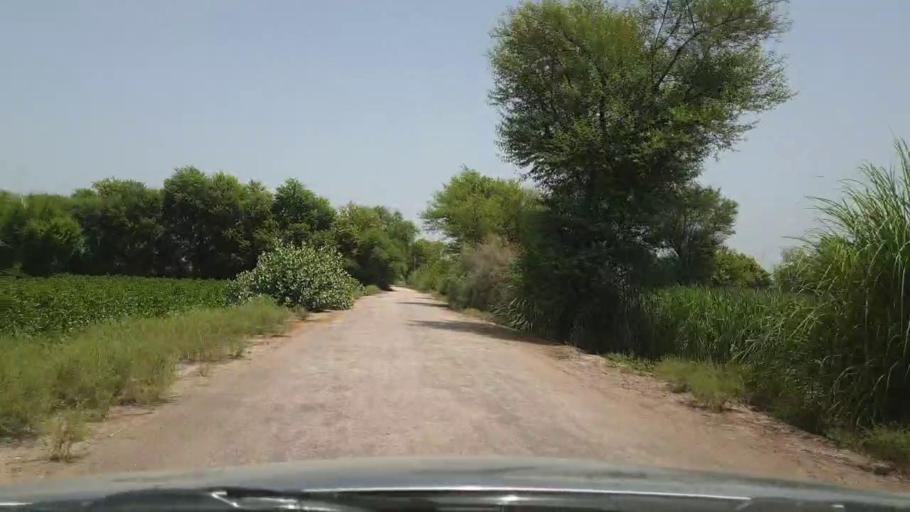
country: PK
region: Sindh
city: Pano Aqil
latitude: 27.8685
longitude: 69.1741
